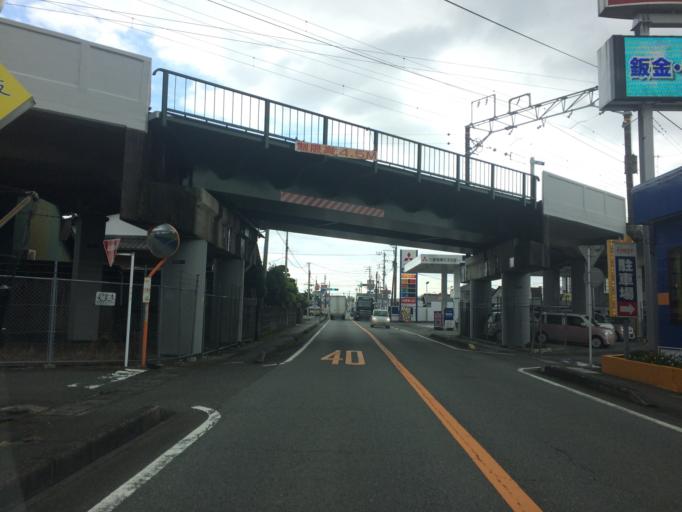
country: JP
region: Shizuoka
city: Fuji
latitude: 35.1715
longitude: 138.6483
